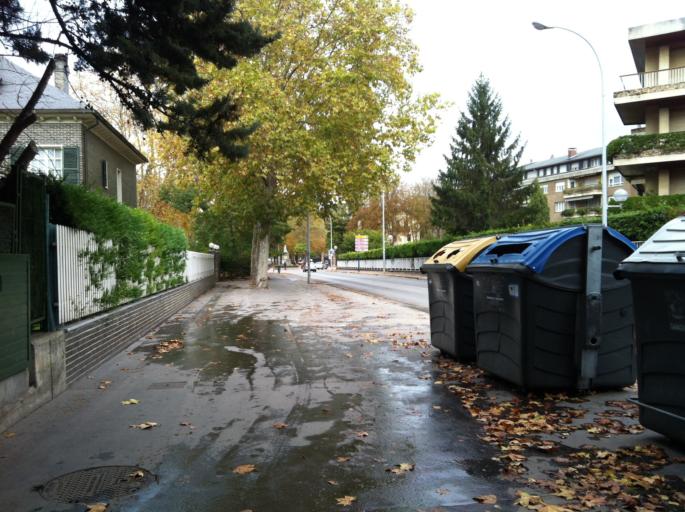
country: ES
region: Basque Country
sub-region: Provincia de Alava
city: Gasteiz / Vitoria
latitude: 42.8394
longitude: -2.6834
